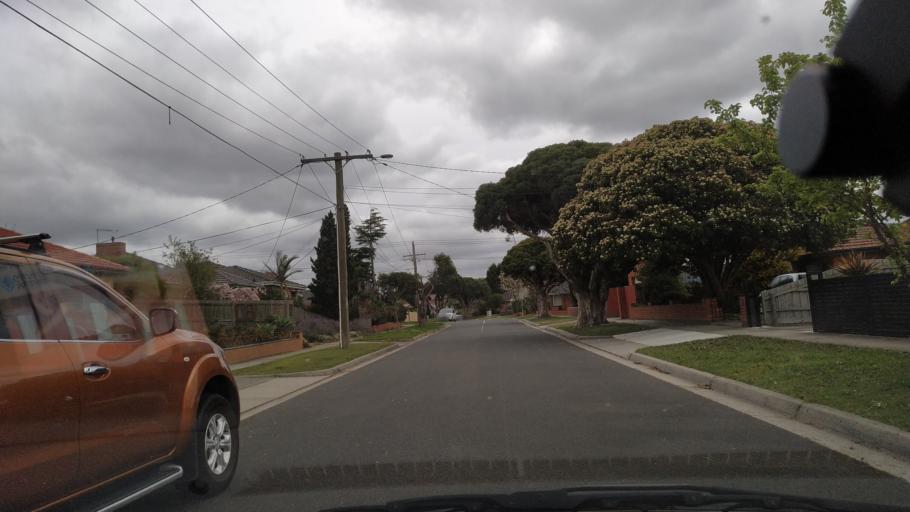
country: AU
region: Victoria
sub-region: Greater Dandenong
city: Dandenong North
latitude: -37.9621
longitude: 145.2053
